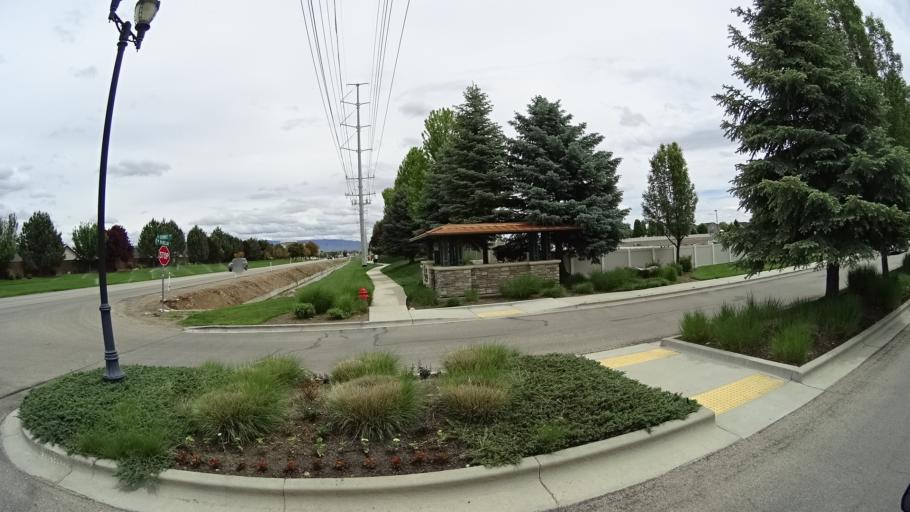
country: US
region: Idaho
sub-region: Ada County
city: Meridian
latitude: 43.6482
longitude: -116.4014
